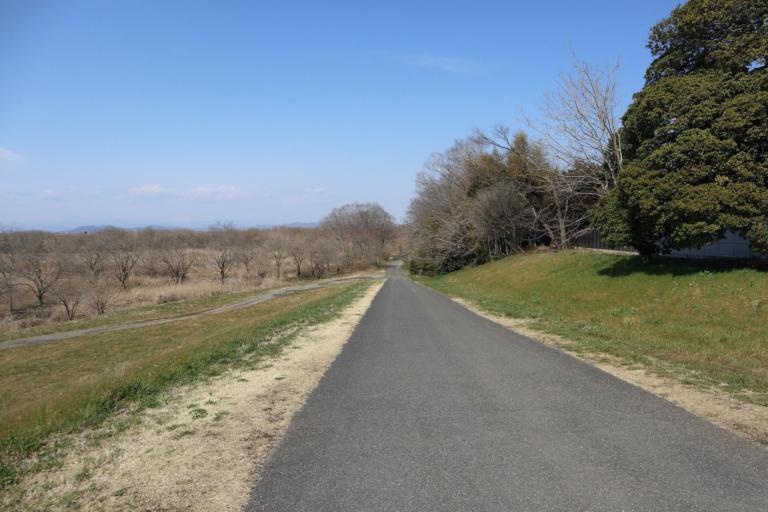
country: JP
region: Ibaraki
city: Koga
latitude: 36.2093
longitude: 139.6979
